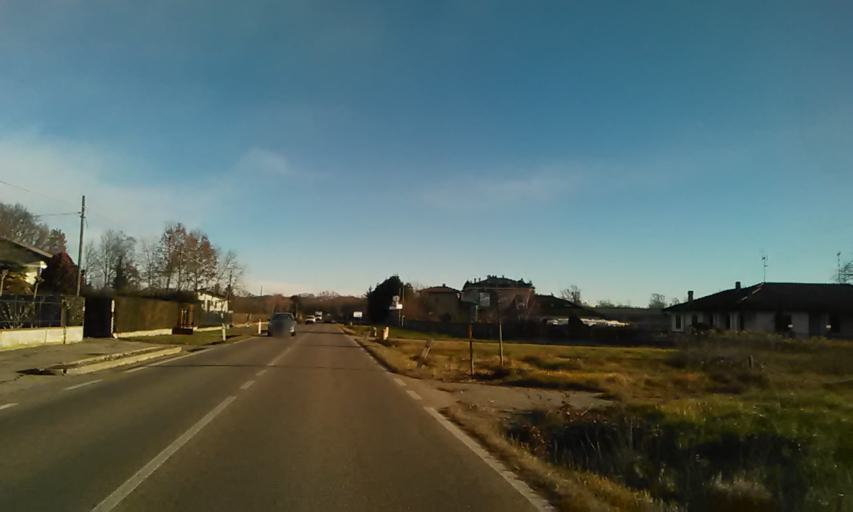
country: IT
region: Piedmont
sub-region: Provincia di Biella
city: Brusnengo
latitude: 45.5832
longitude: 8.2658
